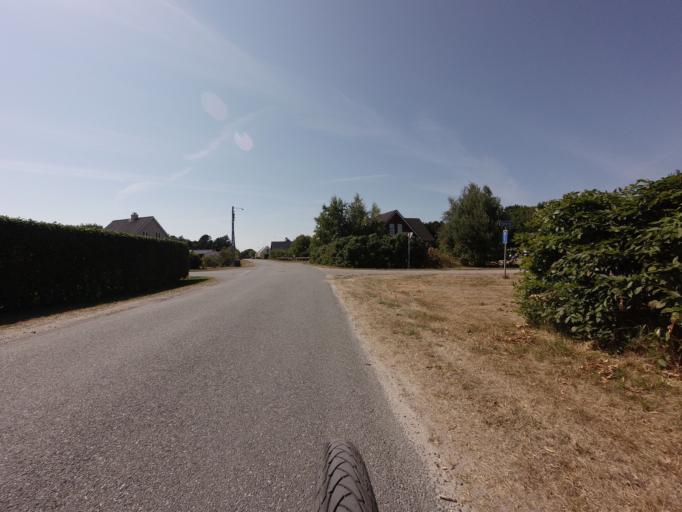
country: DK
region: North Denmark
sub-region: Laeso Kommune
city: Byrum
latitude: 57.2955
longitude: 10.9310
